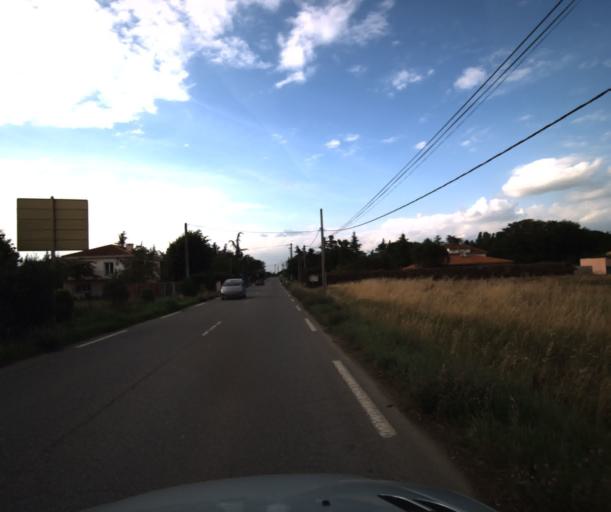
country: FR
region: Midi-Pyrenees
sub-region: Departement de la Haute-Garonne
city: Labarthe-sur-Leze
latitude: 43.4668
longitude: 1.3978
